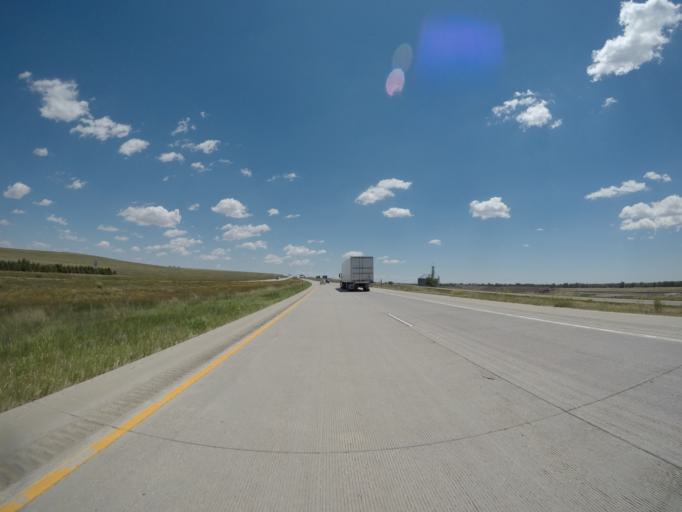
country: US
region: Colorado
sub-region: Lincoln County
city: Limon
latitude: 39.2732
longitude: -103.7346
